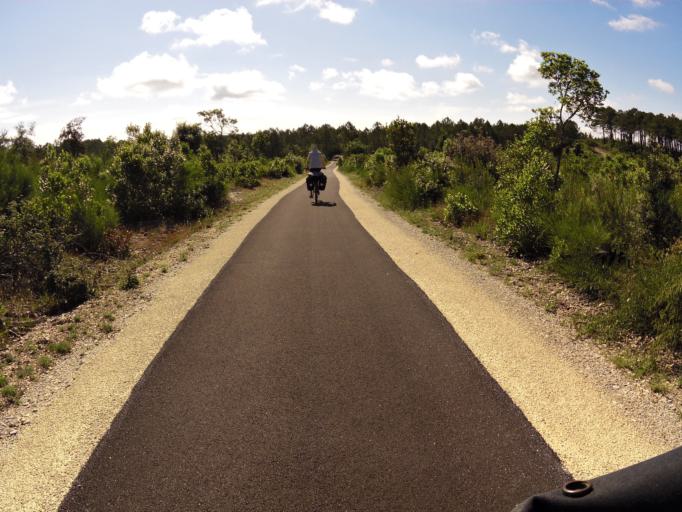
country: FR
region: Aquitaine
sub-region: Departement de la Gironde
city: Lacanau
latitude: 45.0327
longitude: -1.1789
